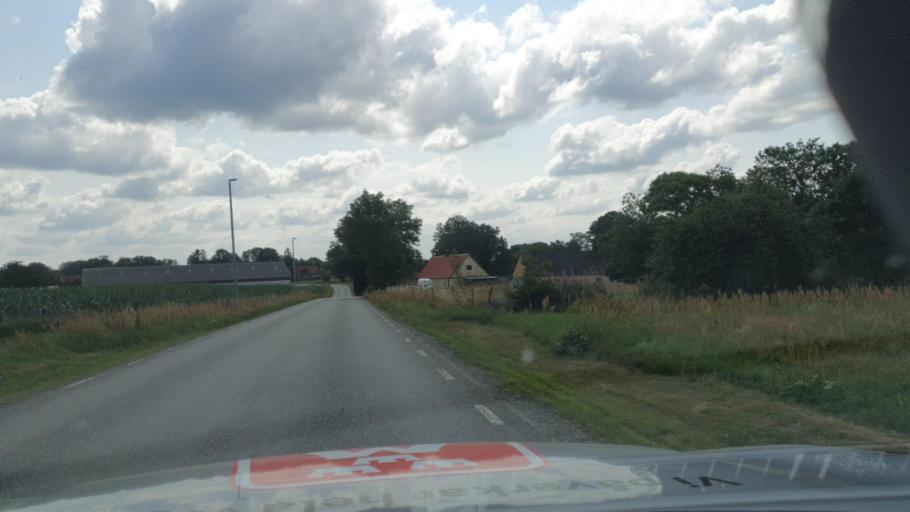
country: SE
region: Skane
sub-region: Hassleholms Kommun
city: Vinslov
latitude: 56.0586
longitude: 13.8359
